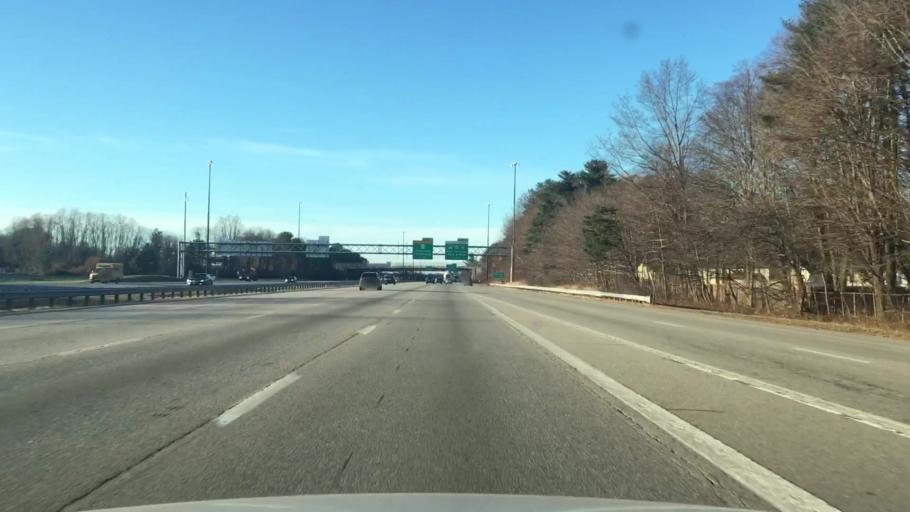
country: US
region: New Hampshire
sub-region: Rockingham County
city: Portsmouth
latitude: 43.0634
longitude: -70.7964
